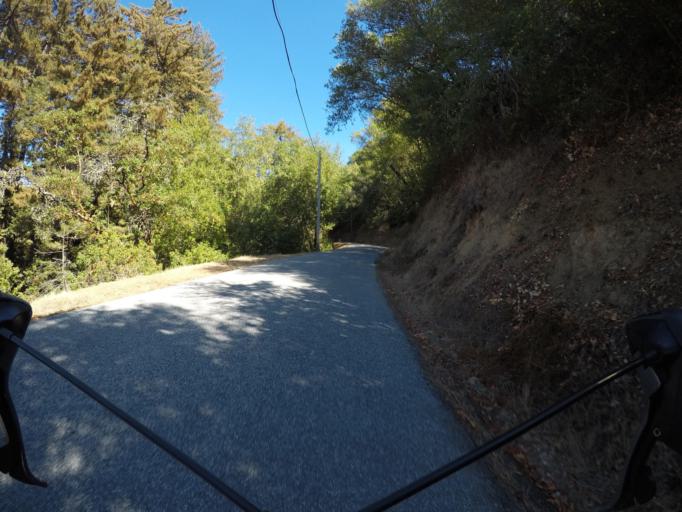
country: US
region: California
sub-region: San Mateo County
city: Portola Valley
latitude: 37.3642
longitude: -122.2569
